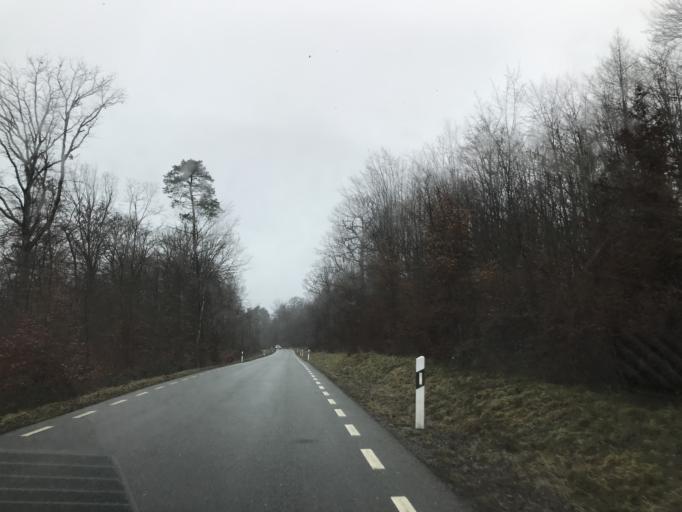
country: DE
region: Baden-Wuerttemberg
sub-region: Regierungsbezirk Stuttgart
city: Weil im Schonbuch
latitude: 48.6120
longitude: 9.0595
